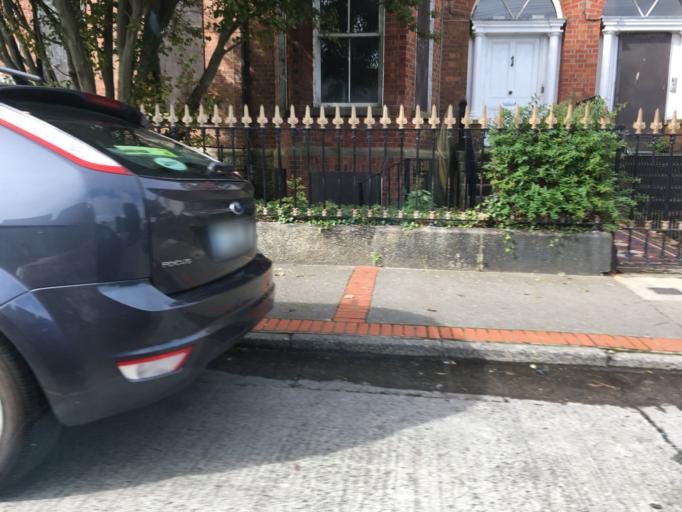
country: IE
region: Leinster
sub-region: Wicklow
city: Bray
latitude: 53.2040
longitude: -6.1064
